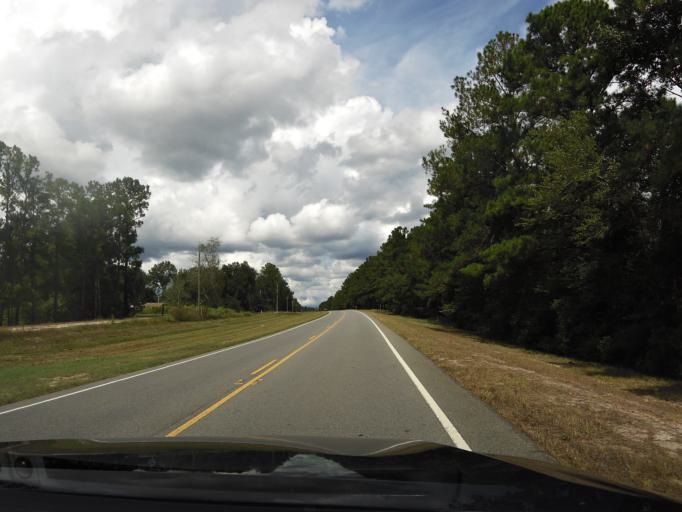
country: US
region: Georgia
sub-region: Brantley County
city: Nahunta
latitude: 31.1014
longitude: -82.0050
